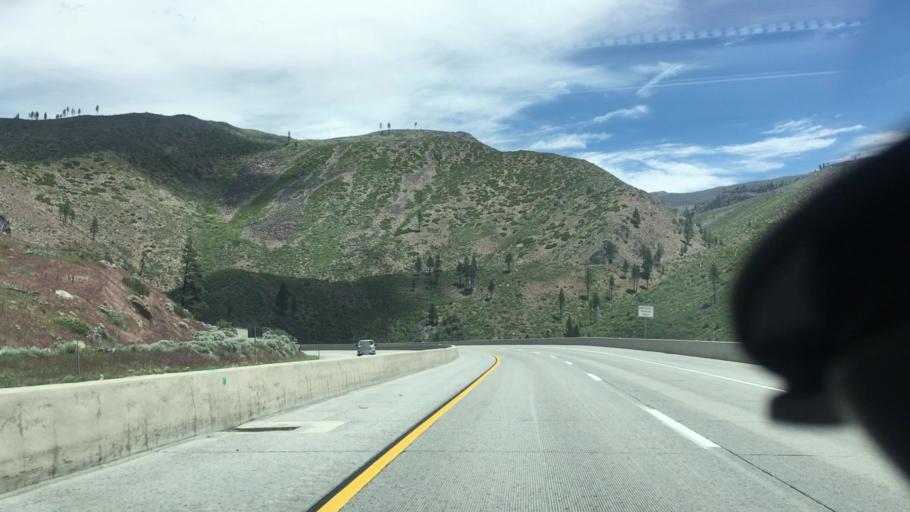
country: US
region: Nevada
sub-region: Washoe County
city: Incline Village
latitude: 39.3780
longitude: -120.0256
